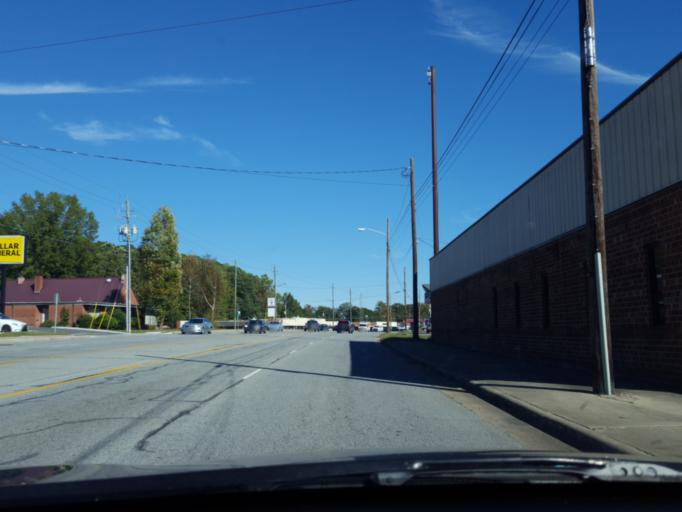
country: US
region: North Carolina
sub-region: Pitt County
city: Greenville
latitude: 35.6032
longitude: -77.3447
